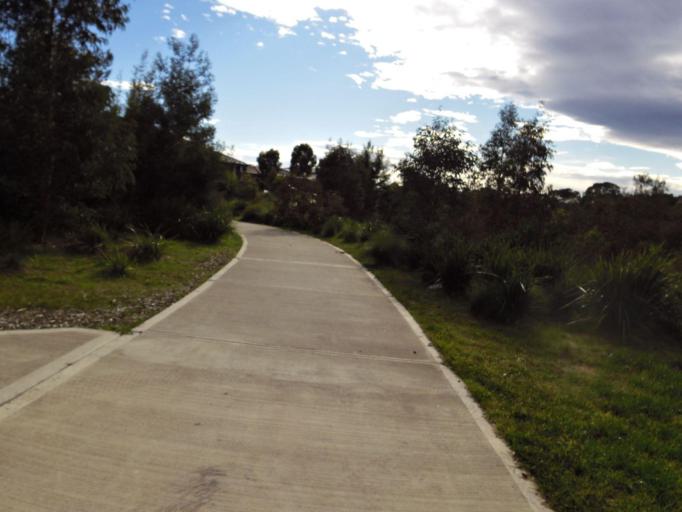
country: AU
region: Victoria
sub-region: Whittlesea
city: Epping
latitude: -37.6158
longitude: 145.0405
